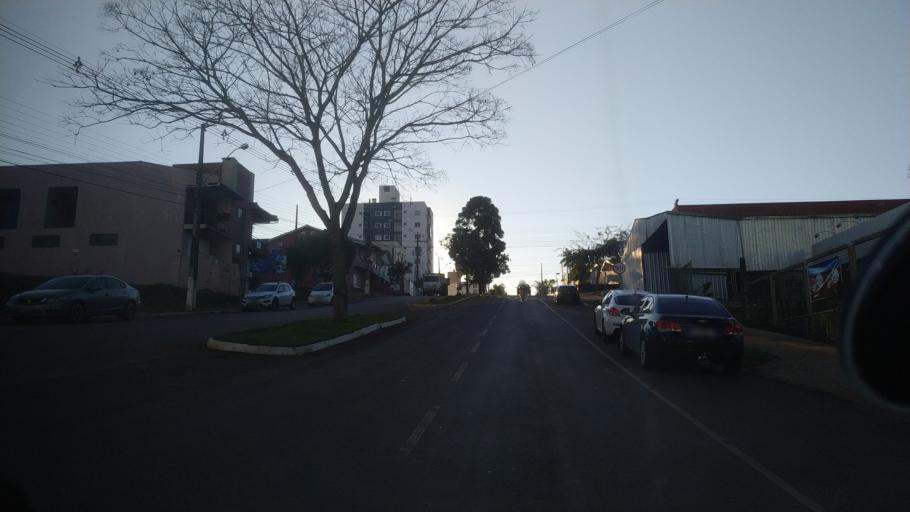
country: BR
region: Santa Catarina
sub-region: Chapeco
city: Chapeco
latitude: -27.0891
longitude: -52.5887
